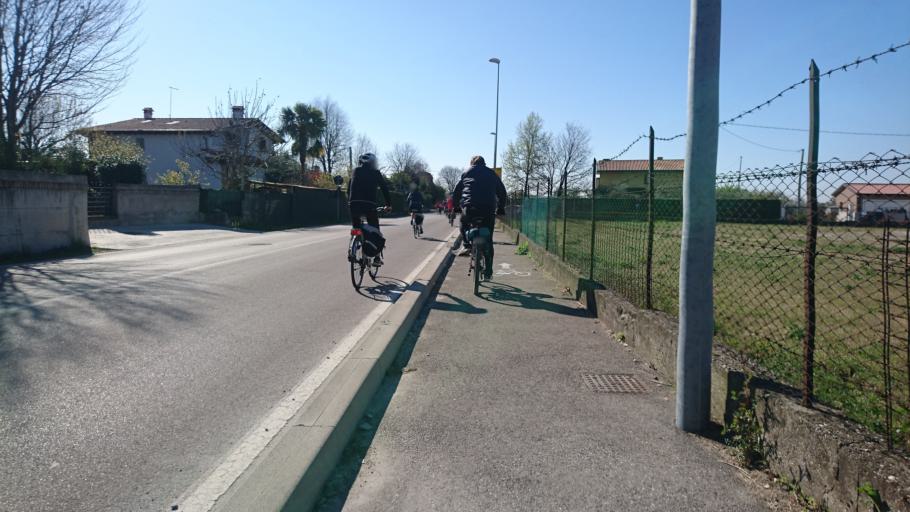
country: IT
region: Veneto
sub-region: Provincia di Vicenza
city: Bassano del Grappa
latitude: 45.7384
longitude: 11.7407
